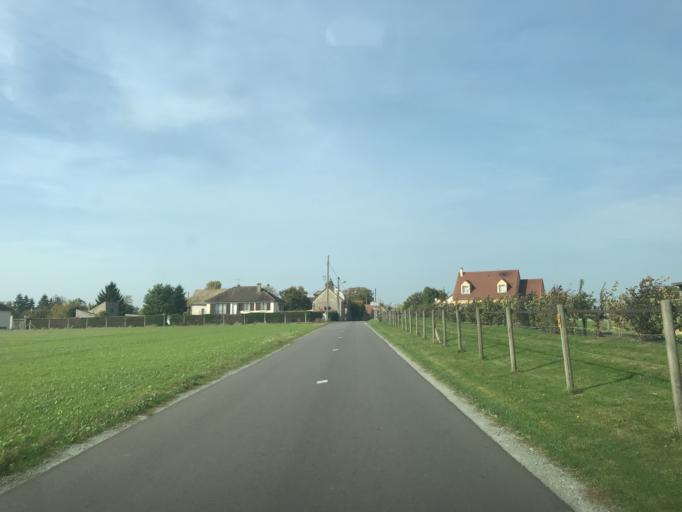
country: FR
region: Haute-Normandie
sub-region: Departement de l'Eure
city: La Chapelle-Reanville
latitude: 49.0696
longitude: 1.4039
